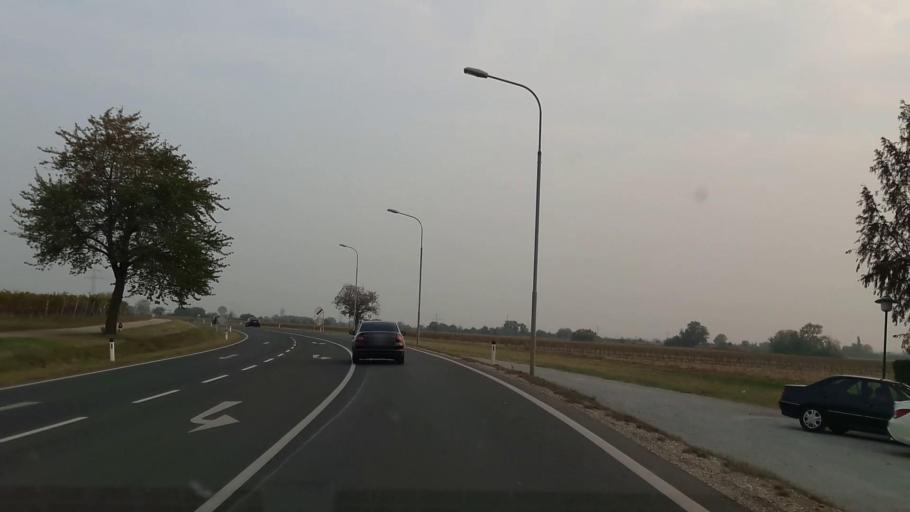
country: AT
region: Burgenland
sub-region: Politischer Bezirk Neusiedl am See
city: Weiden am See
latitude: 47.9188
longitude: 16.8785
